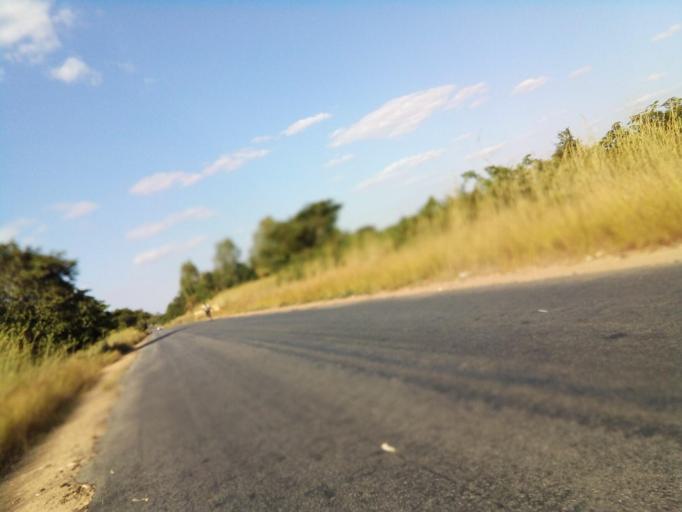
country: MZ
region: Zambezia
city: Quelimane
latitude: -17.5754
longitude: 36.6280
